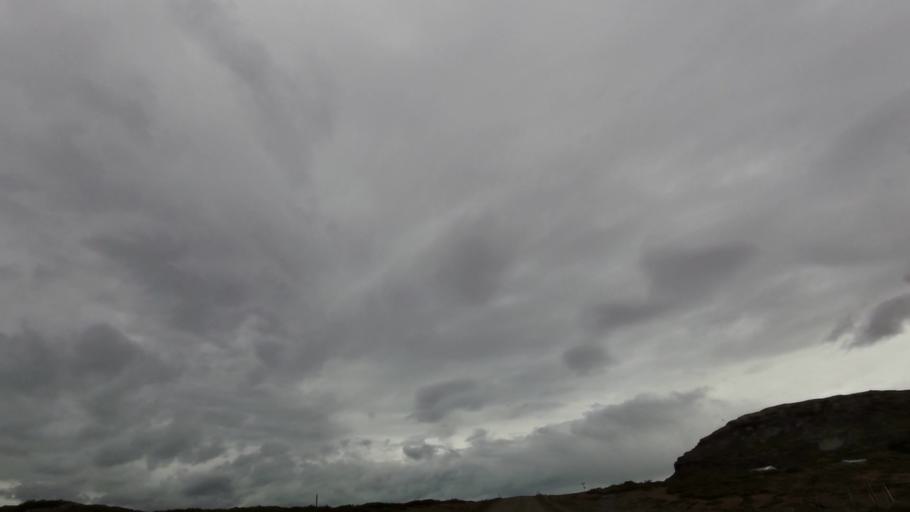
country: IS
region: West
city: Stykkisholmur
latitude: 65.0394
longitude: -22.3897
